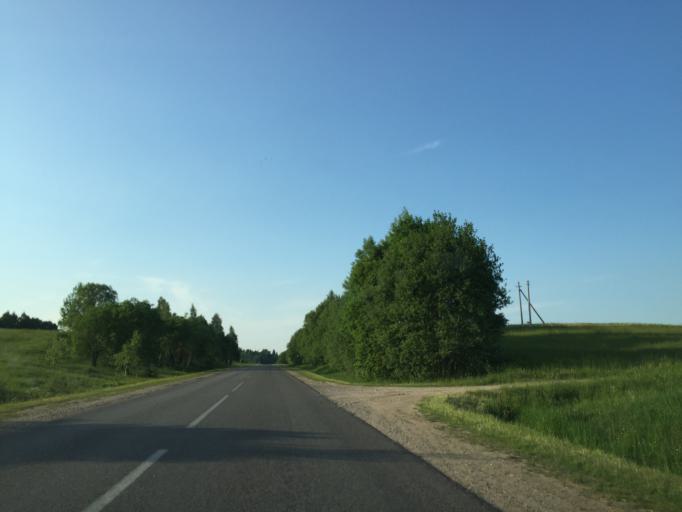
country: LT
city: Plateliai
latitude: 56.0541
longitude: 21.8194
